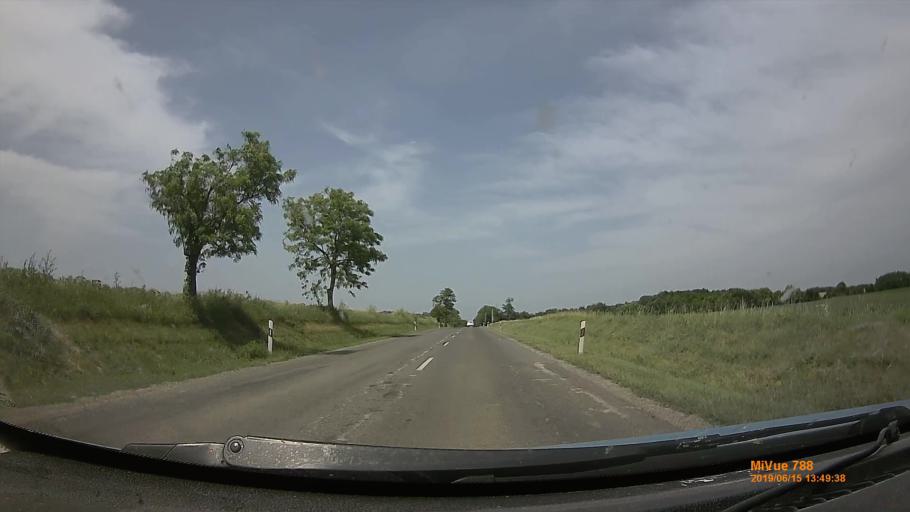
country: HU
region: Tolna
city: Iregszemcse
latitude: 46.7323
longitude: 18.1666
